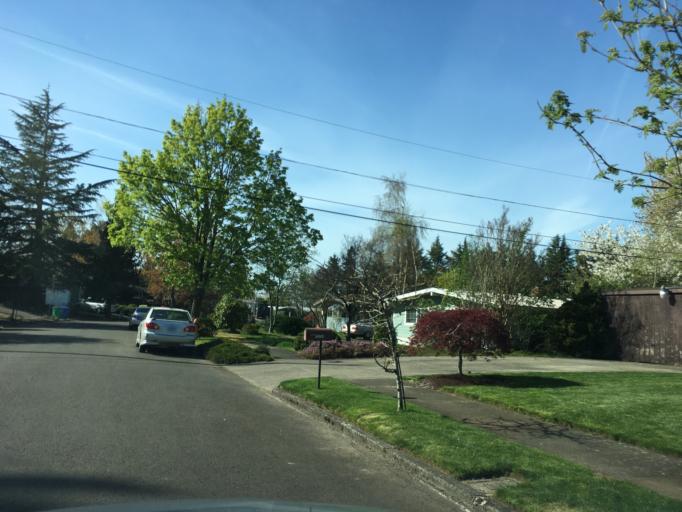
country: US
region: Oregon
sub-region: Multnomah County
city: Lents
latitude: 45.5412
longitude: -122.5253
